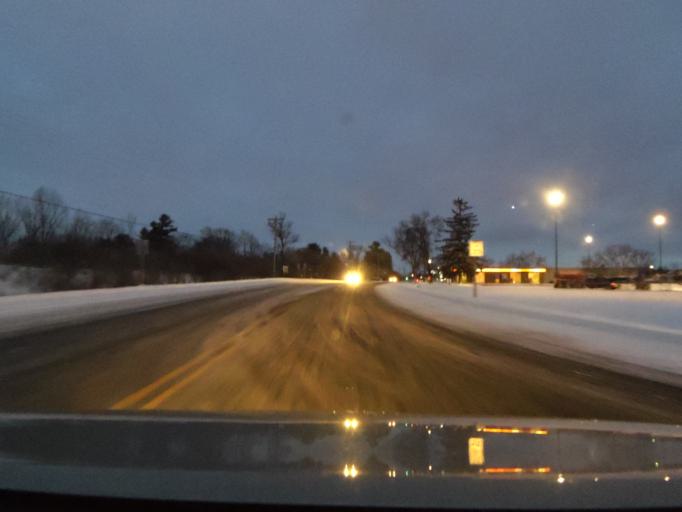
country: US
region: Wisconsin
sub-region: Dunn County
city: Menomonie
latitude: 44.9055
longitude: -91.9379
